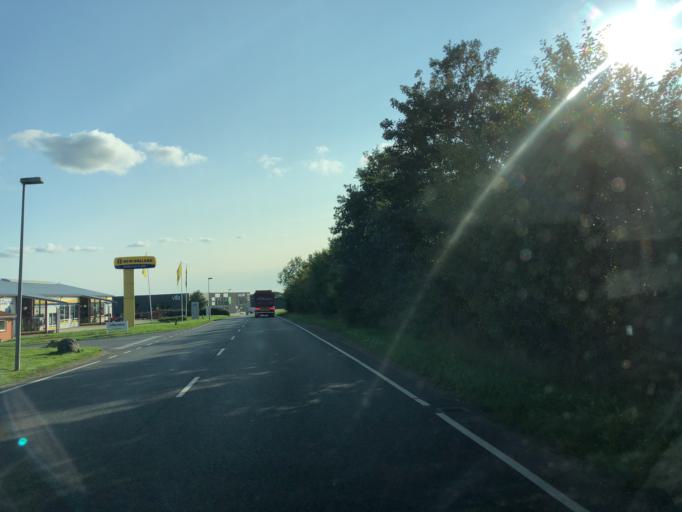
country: DK
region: Central Jutland
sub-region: Viborg Kommune
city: Viborg
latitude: 56.4596
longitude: 9.3626
